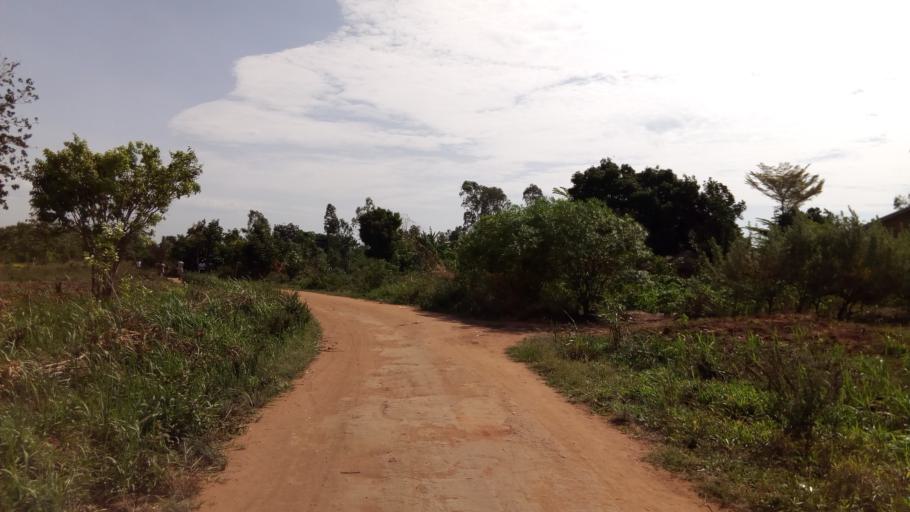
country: UG
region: Northern Region
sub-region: Gulu District
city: Gulu
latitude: 2.7959
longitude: 32.3273
